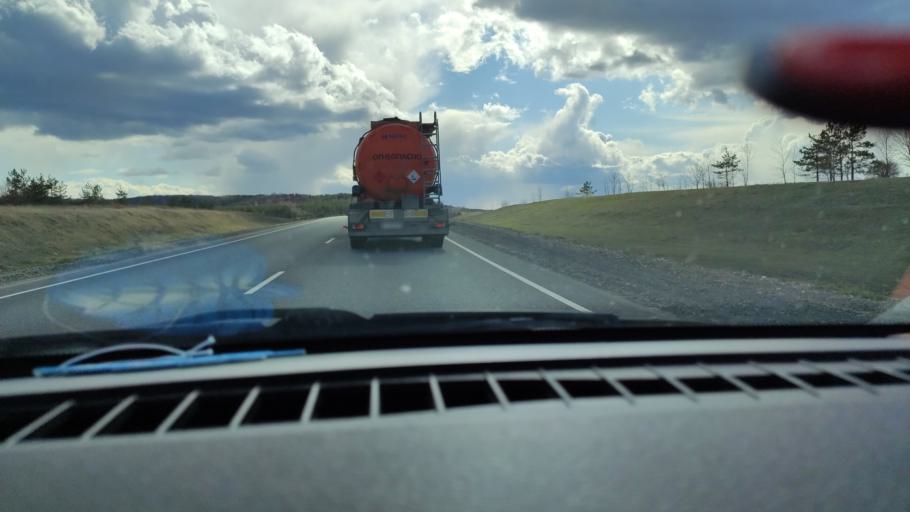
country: RU
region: Saratov
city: Khvalynsk
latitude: 52.5480
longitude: 48.0705
